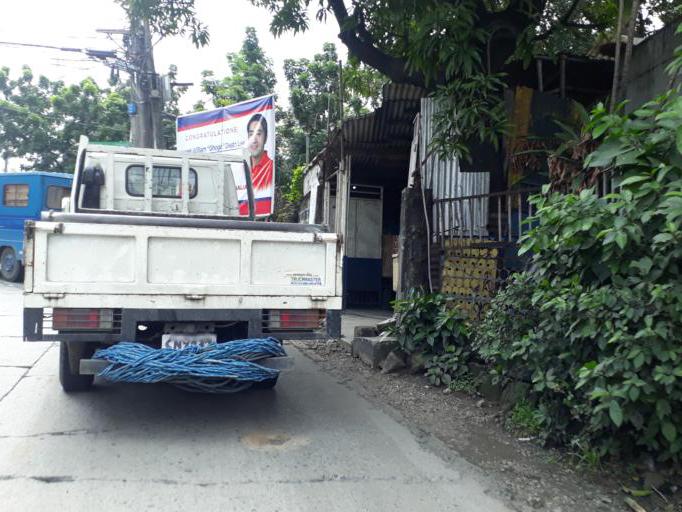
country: PH
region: Calabarzon
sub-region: Province of Rizal
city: Valenzuela
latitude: 14.7042
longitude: 121.0048
